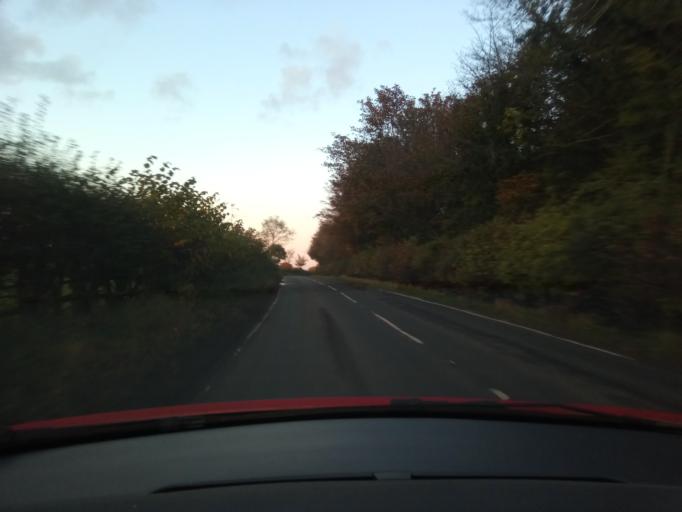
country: GB
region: England
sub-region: Northumberland
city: Bardon Mill
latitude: 54.9592
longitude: -2.2535
